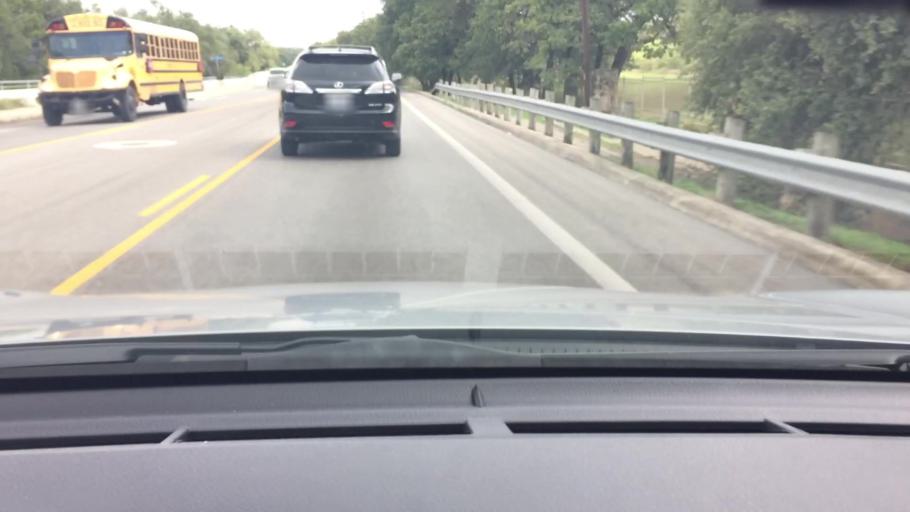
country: US
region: Texas
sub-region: Bexar County
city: Shavano Park
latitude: 29.5556
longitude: -98.5470
